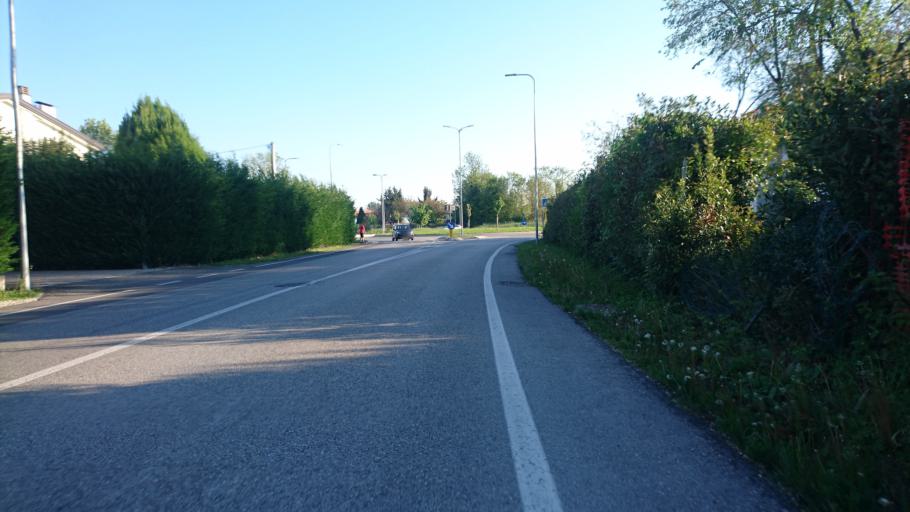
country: IT
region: Veneto
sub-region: Provincia di Padova
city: Noventa
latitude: 45.4159
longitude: 11.9370
